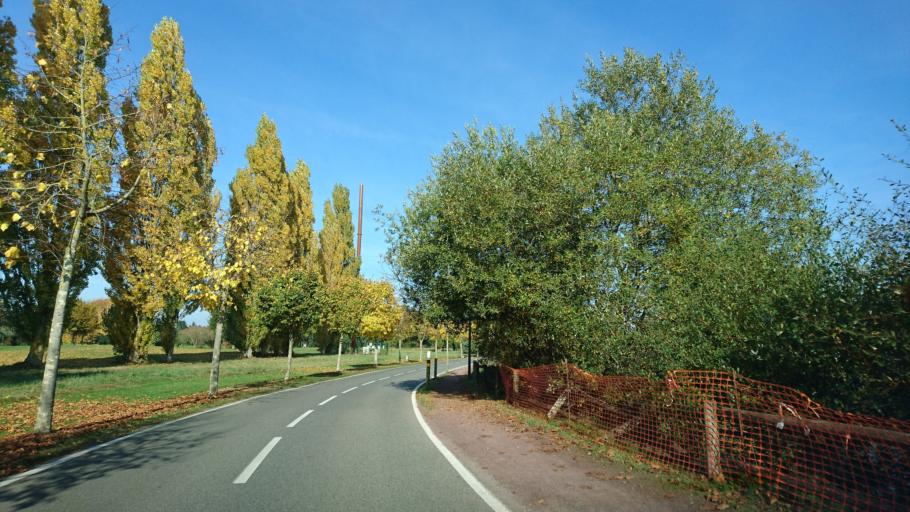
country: FR
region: Brittany
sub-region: Departement d'Ille-et-Vilaine
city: Bruz
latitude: 48.0349
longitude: -1.7655
